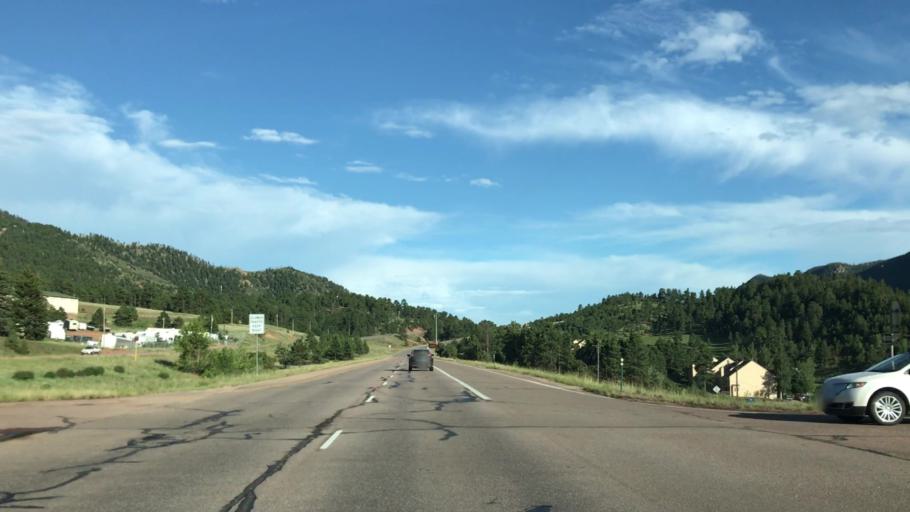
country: US
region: Colorado
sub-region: El Paso County
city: Cascade-Chipita Park
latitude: 38.9420
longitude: -105.0169
